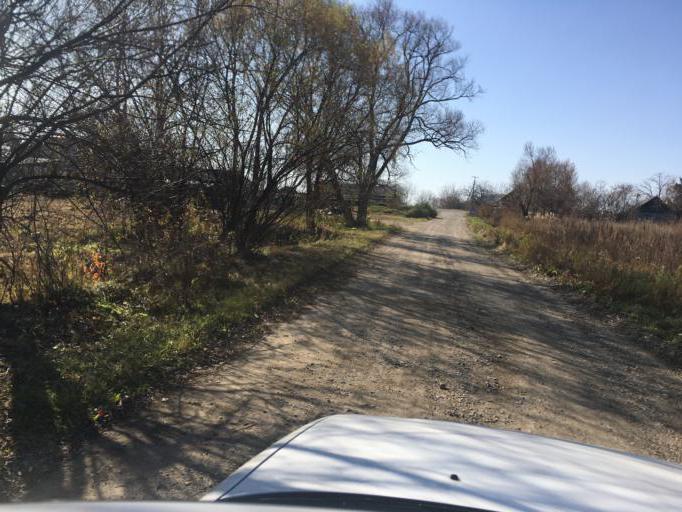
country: RU
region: Primorskiy
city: Dal'nerechensk
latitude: 45.9166
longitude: 133.7874
